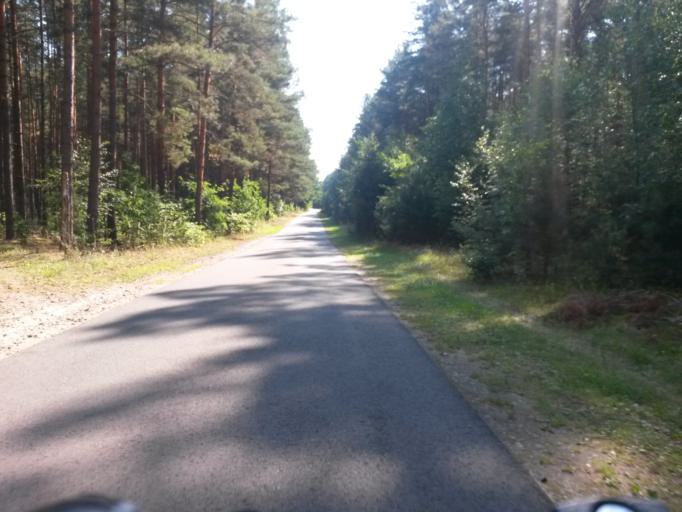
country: DE
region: Brandenburg
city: Templin
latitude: 53.0480
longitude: 13.4806
